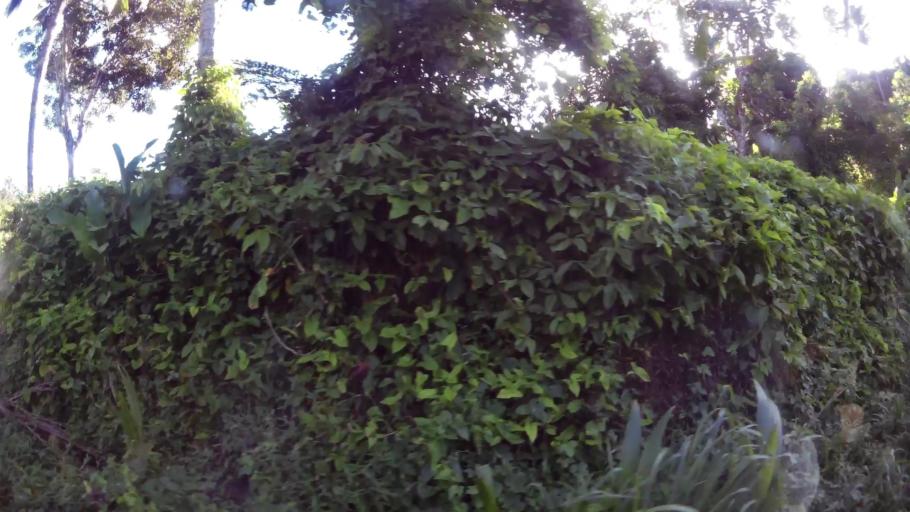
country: DM
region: Saint John
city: Portsmouth
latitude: 15.5796
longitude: -61.4239
